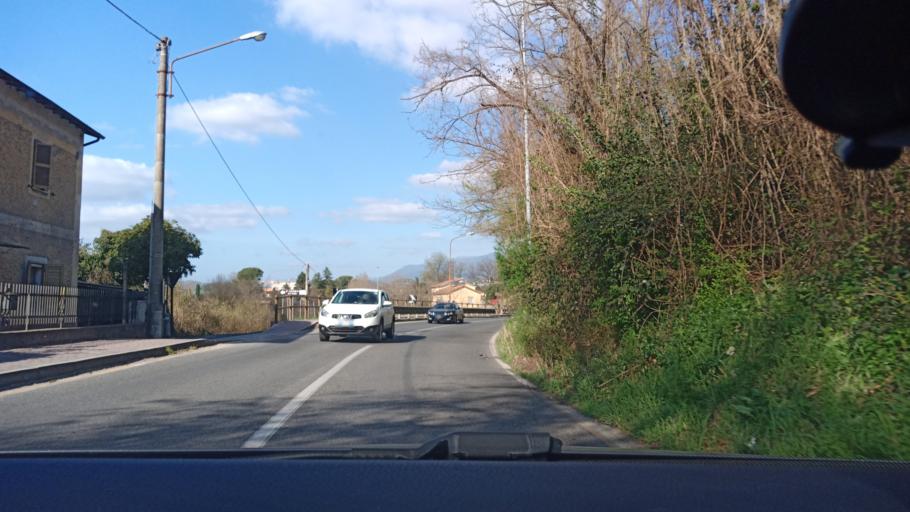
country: IT
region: Latium
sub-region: Citta metropolitana di Roma Capitale
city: Torrita Tiberina
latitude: 42.2472
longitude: 12.6352
